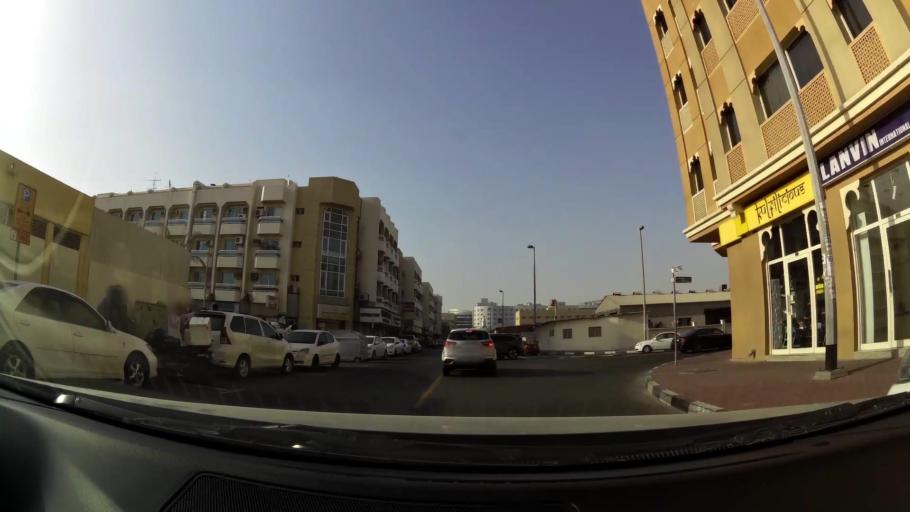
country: AE
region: Ash Shariqah
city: Sharjah
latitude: 25.2482
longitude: 55.3070
